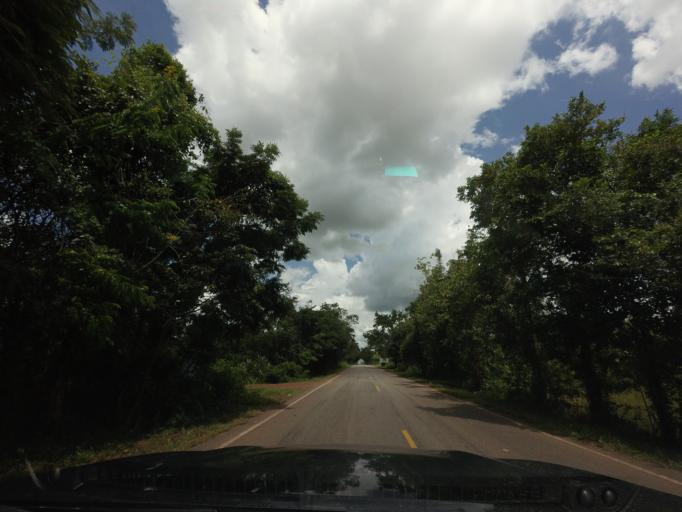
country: TH
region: Changwat Udon Thani
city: Phibun Rak
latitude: 17.6000
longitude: 103.0655
